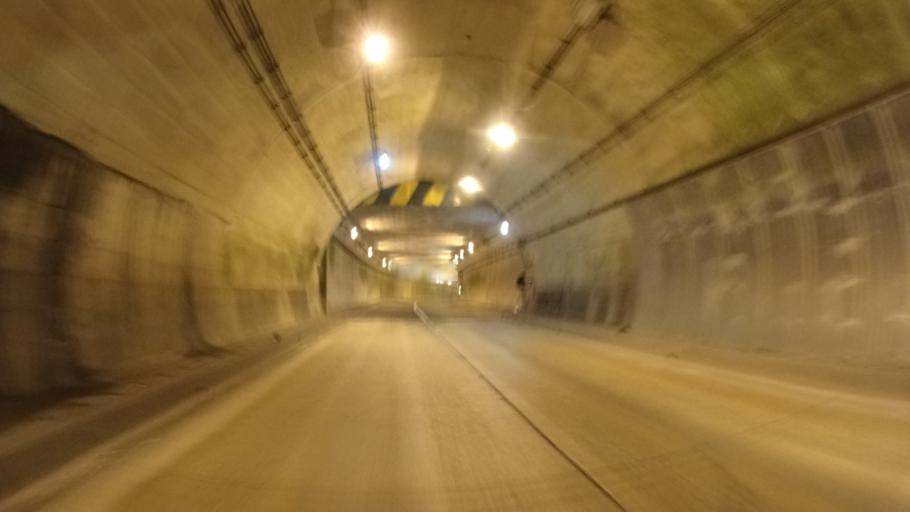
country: JP
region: Ishikawa
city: Tsurugi-asahimachi
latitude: 36.3678
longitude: 136.5876
